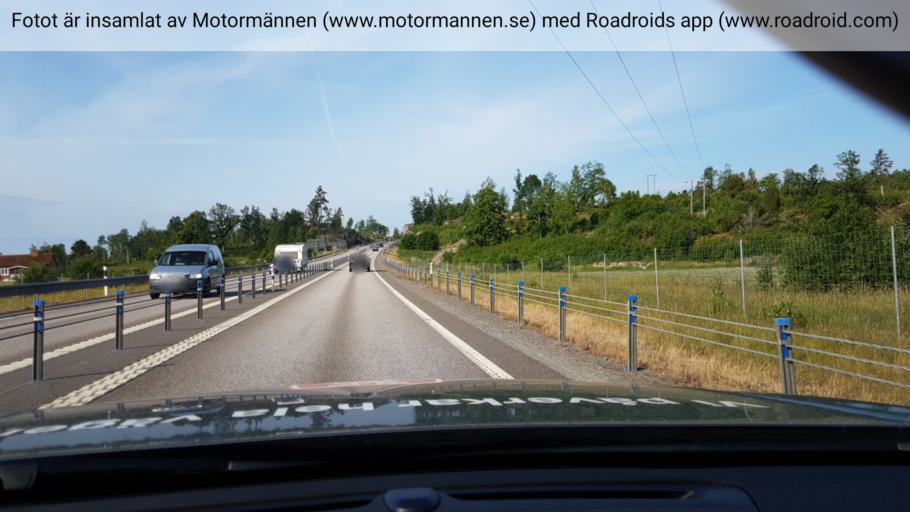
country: SE
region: OErebro
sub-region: Askersunds Kommun
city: Askersund
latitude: 58.8233
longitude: 14.8852
